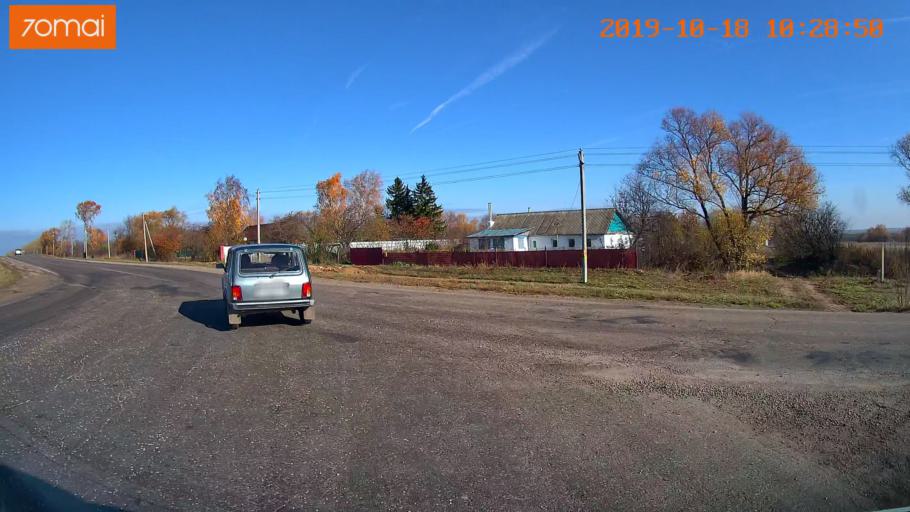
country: RU
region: Tula
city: Kurkino
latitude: 53.4473
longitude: 38.6604
